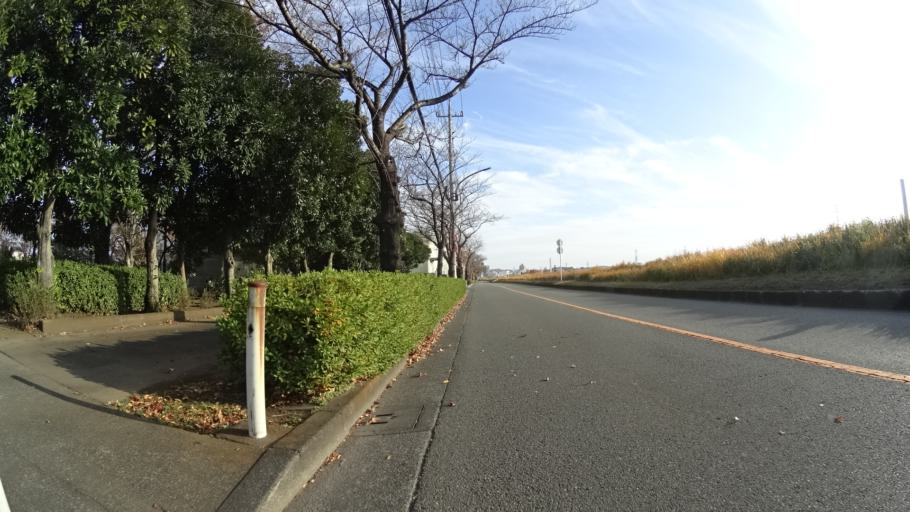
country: JP
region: Tokyo
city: Hino
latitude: 35.6705
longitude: 139.4316
